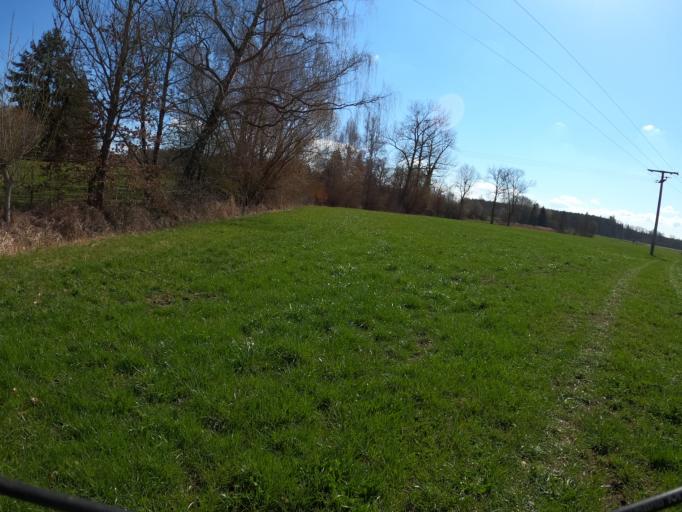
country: DE
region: Bavaria
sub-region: Swabia
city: Nersingen
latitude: 48.4029
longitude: 10.1400
